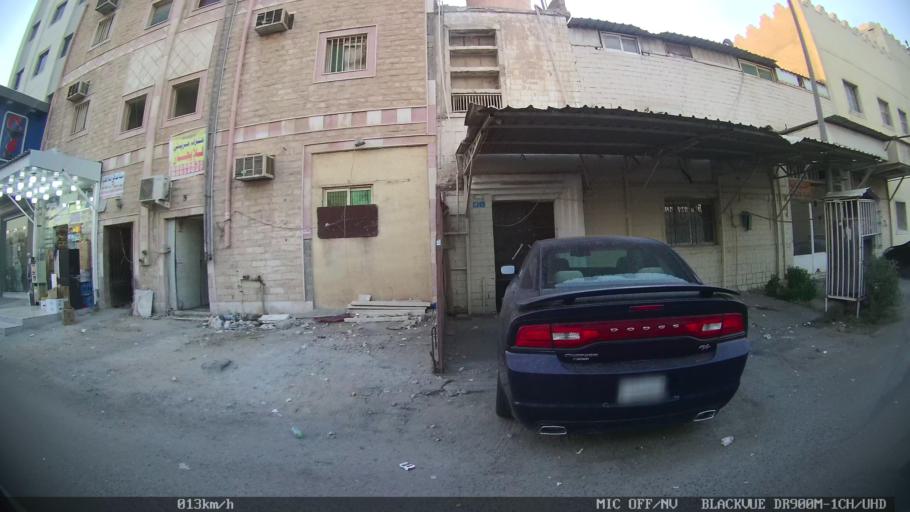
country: KW
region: Al Farwaniyah
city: Janub as Surrah
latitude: 29.2841
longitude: 47.9792
